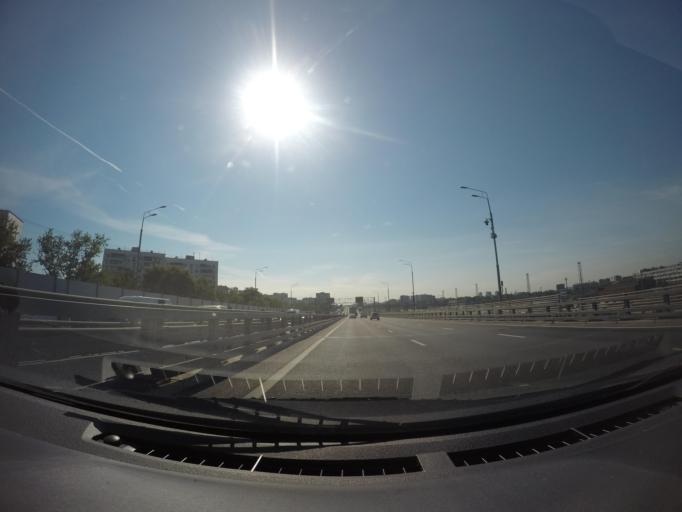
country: RU
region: Moscow
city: Ryazanskiy
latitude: 55.7438
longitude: 37.7522
